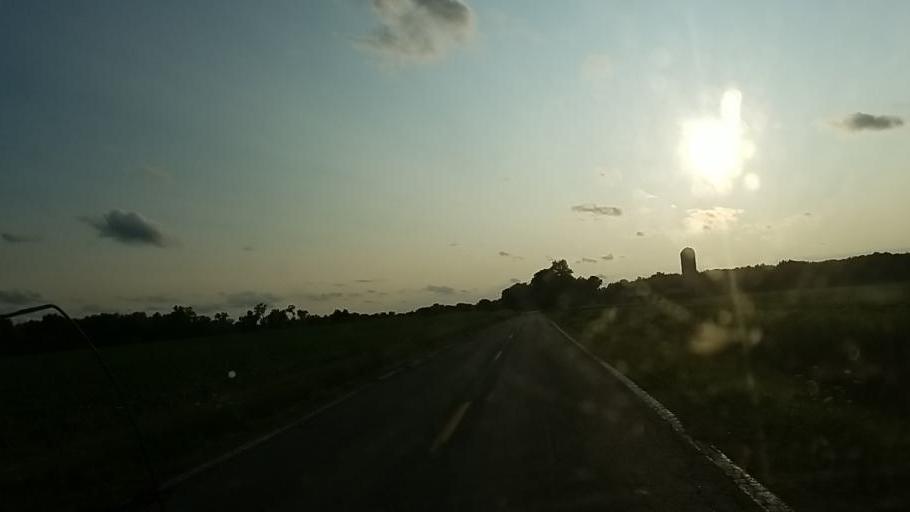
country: US
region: Michigan
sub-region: Montcalm County
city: Howard City
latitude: 43.3591
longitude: -85.3849
